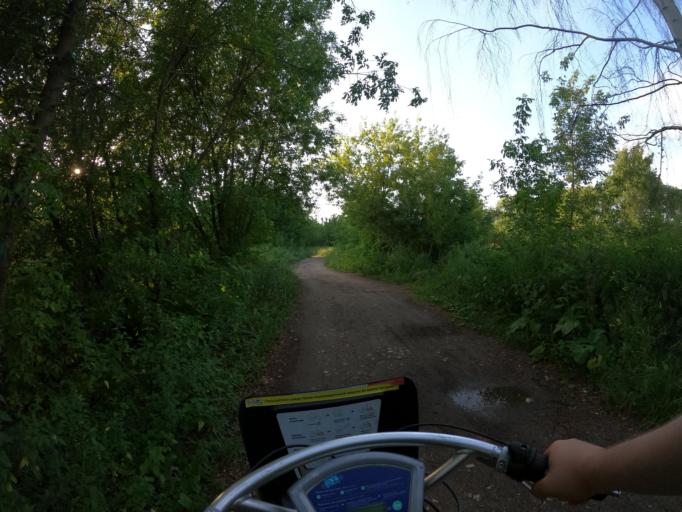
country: RU
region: Moscow
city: Strogino
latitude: 55.8229
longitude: 37.4072
